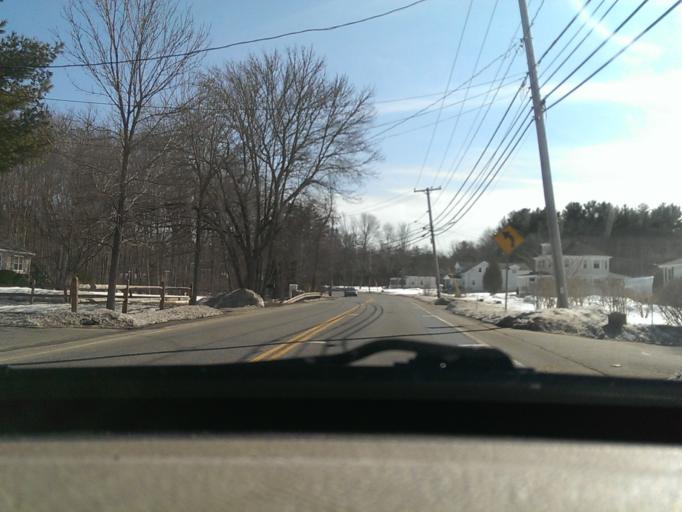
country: US
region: Massachusetts
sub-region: Bristol County
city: Head of Westport
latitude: 41.6462
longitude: -71.0403
